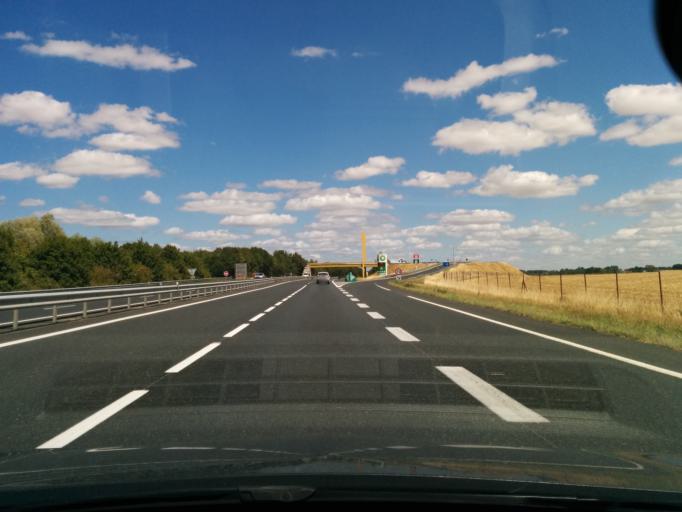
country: FR
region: Centre
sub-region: Departement de l'Indre
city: Vatan
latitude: 47.0880
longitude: 1.8417
